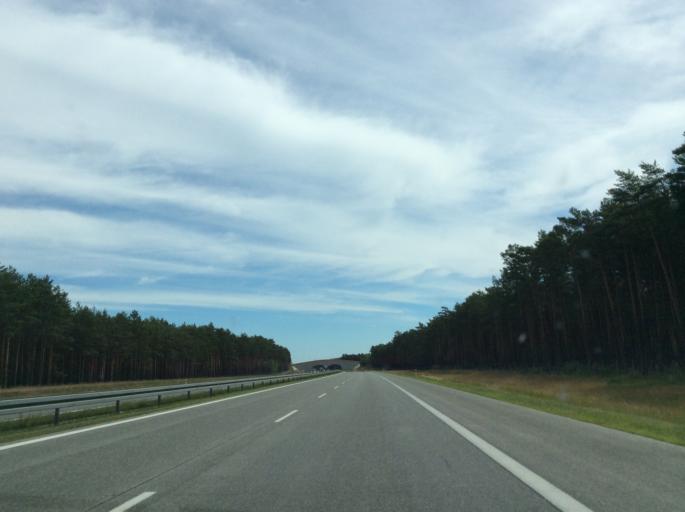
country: PL
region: Lubusz
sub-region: Powiat swiebodzinski
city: Szczaniec
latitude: 52.2980
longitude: 15.7276
